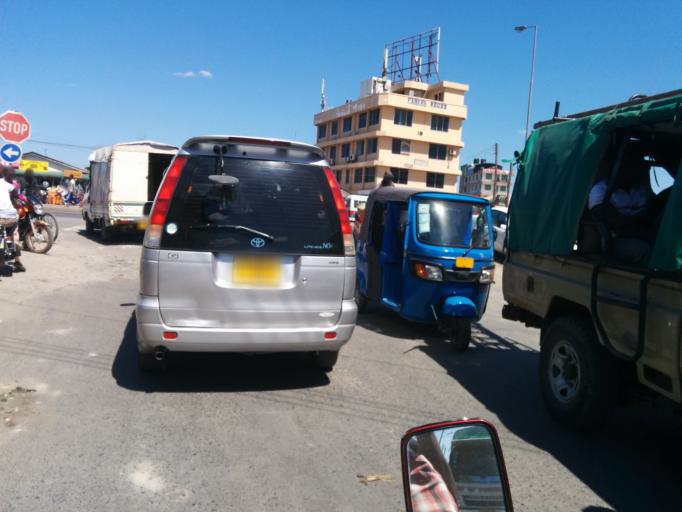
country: TZ
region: Dar es Salaam
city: Magomeni
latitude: -6.7985
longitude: 39.2333
